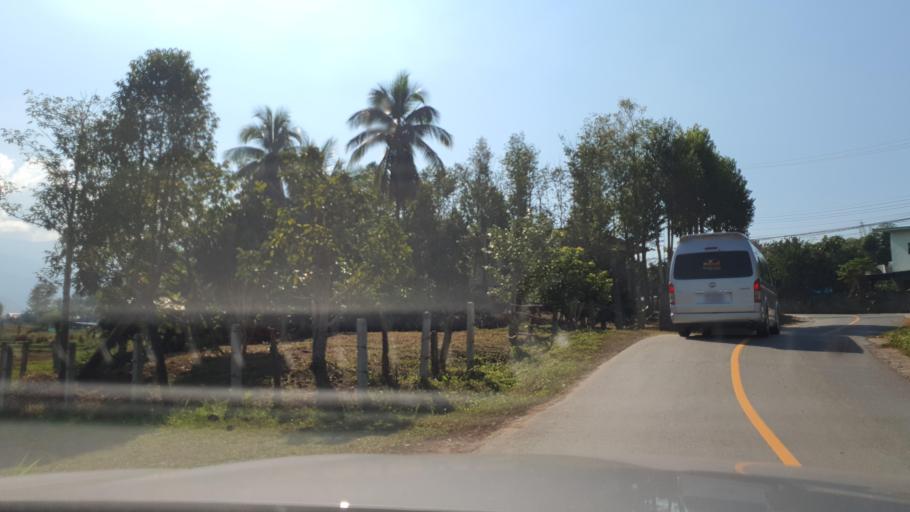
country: TH
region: Nan
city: Pua
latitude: 19.1622
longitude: 100.9292
